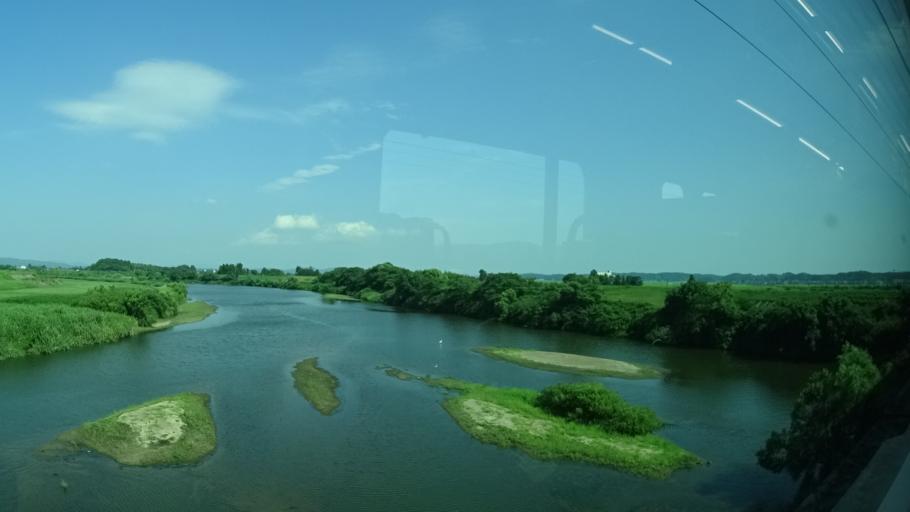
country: JP
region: Miyagi
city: Kogota
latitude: 38.5287
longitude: 141.0653
